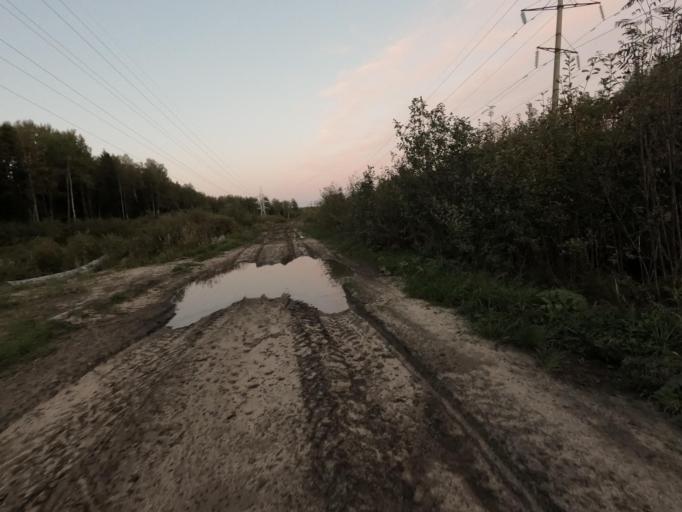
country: RU
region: Leningrad
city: Pavlovo
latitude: 59.7732
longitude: 30.8654
